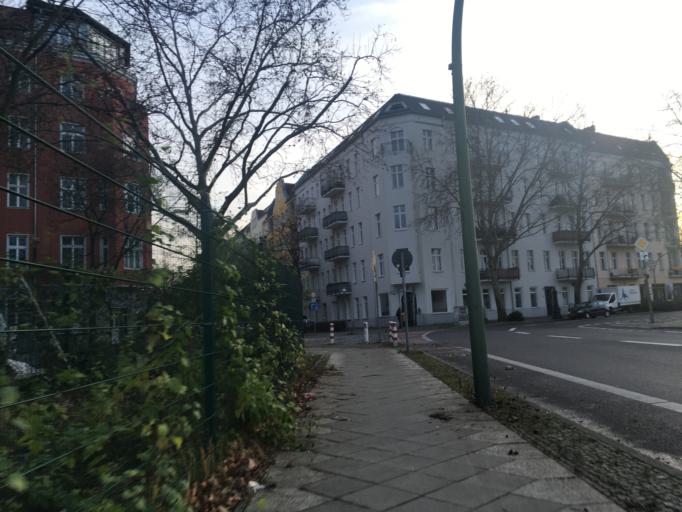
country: DE
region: Berlin
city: Moabit
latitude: 52.5345
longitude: 13.3415
